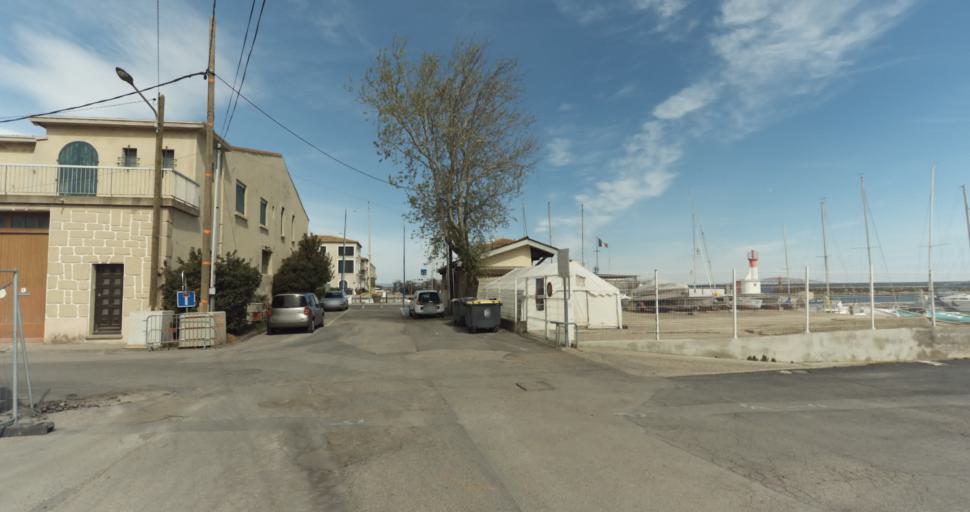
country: FR
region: Languedoc-Roussillon
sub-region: Departement de l'Herault
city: Marseillan
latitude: 43.3524
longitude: 3.5340
